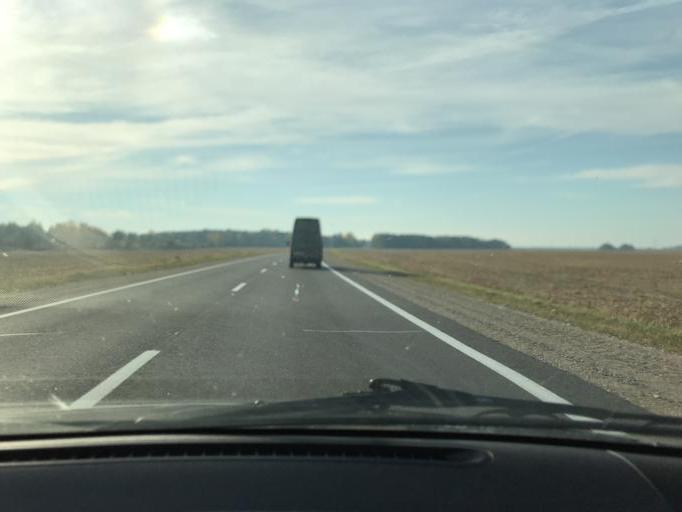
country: BY
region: Brest
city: Horad Pinsk
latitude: 52.1482
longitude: 25.9080
